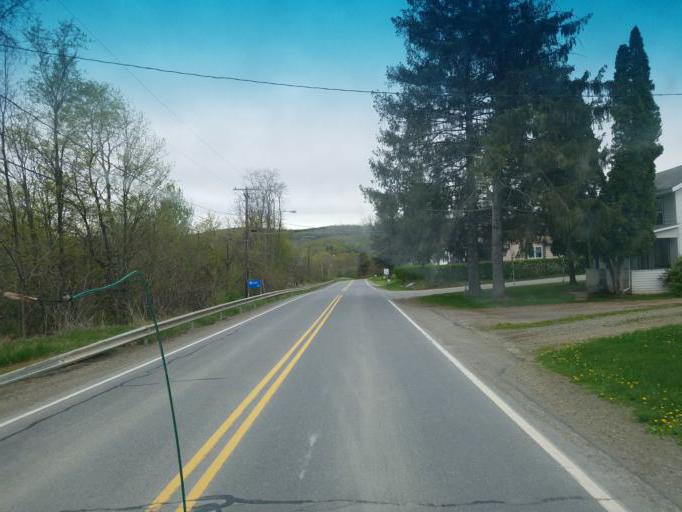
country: US
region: Pennsylvania
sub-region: Tioga County
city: Westfield
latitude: 41.8701
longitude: -77.5240
